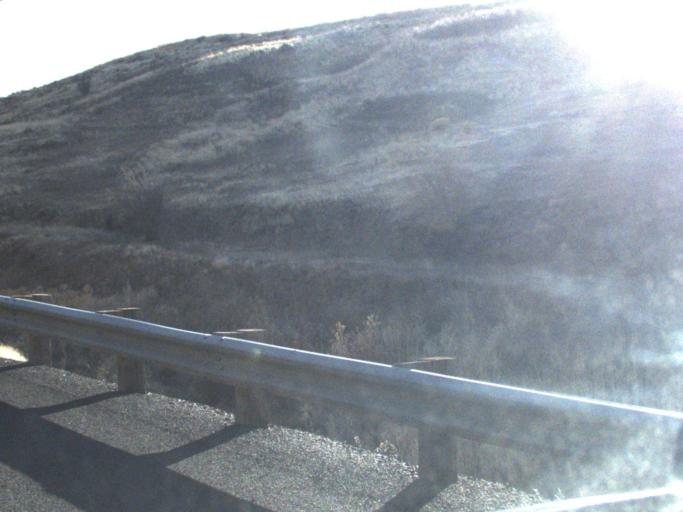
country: US
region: Washington
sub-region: Garfield County
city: Pomeroy
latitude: 46.4465
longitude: -117.4637
